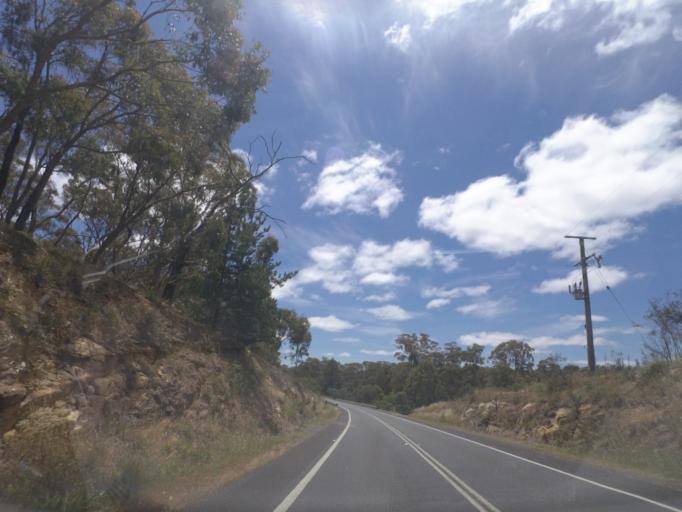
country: AU
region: Victoria
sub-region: Mount Alexander
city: Castlemaine
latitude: -37.2903
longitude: 144.1632
